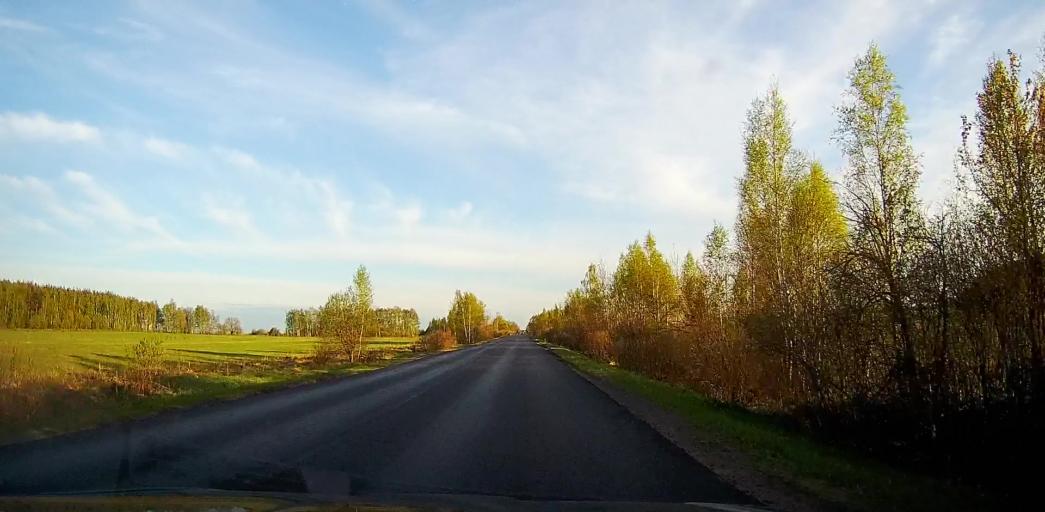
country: RU
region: Moskovskaya
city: Bronnitsy
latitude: 55.2821
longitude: 38.2175
